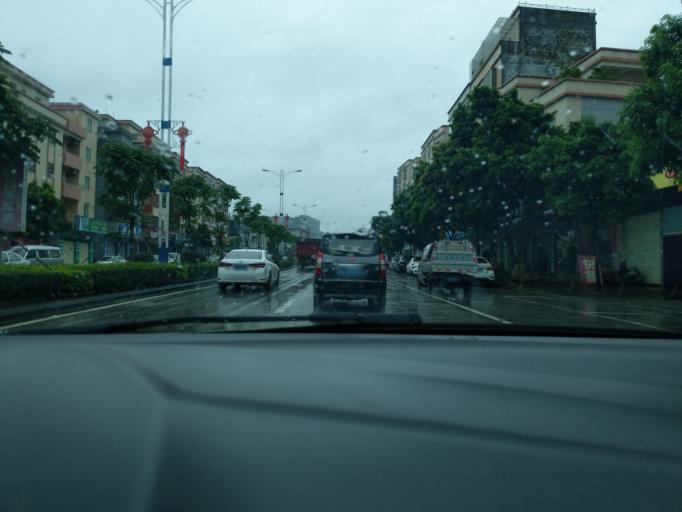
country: CN
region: Guangdong
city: Pingshi
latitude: 22.1980
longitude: 112.3322
